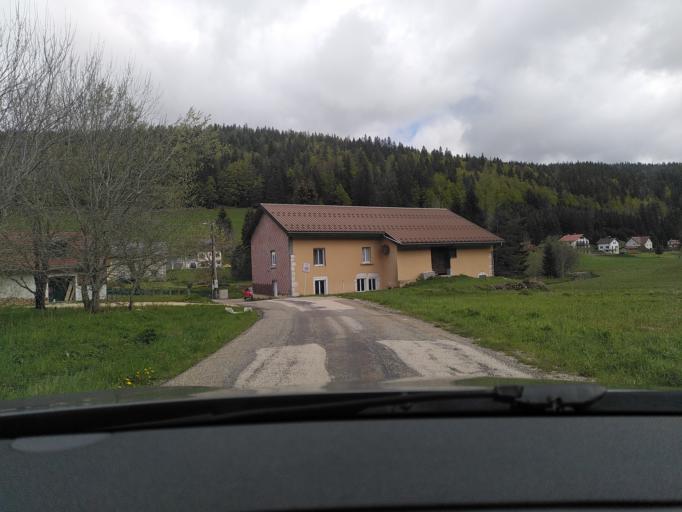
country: FR
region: Franche-Comte
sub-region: Departement du Jura
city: Les Rousses
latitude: 46.5315
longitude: 6.1300
